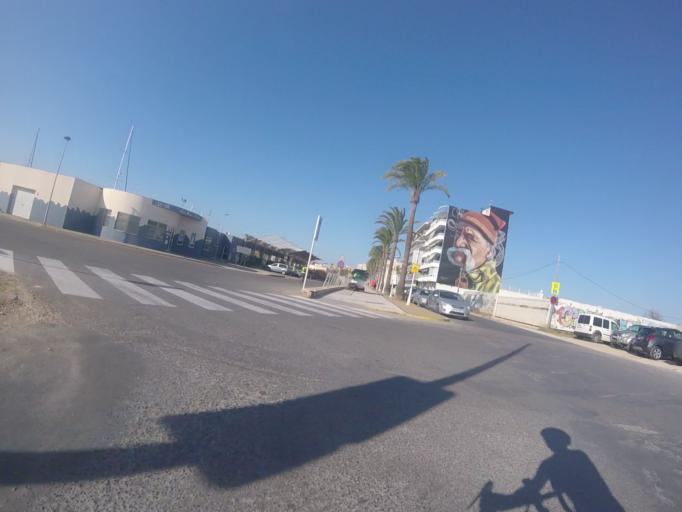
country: ES
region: Valencia
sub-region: Provincia de Castello
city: Benicarlo
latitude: 40.4172
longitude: 0.4352
